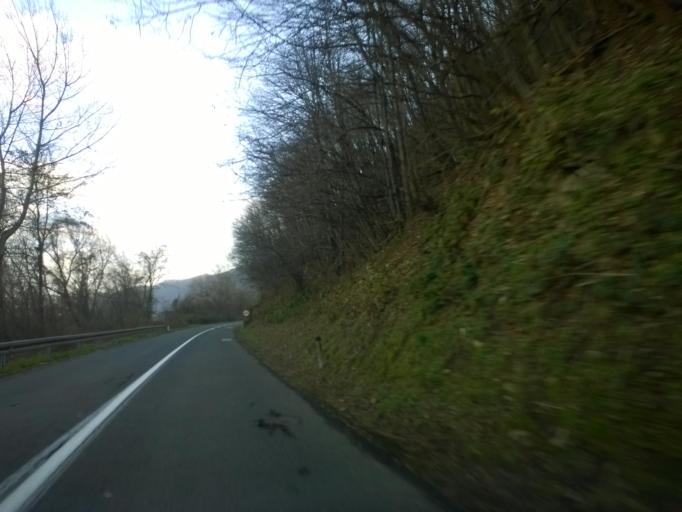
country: RS
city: Radenka
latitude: 44.6534
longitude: 21.7982
